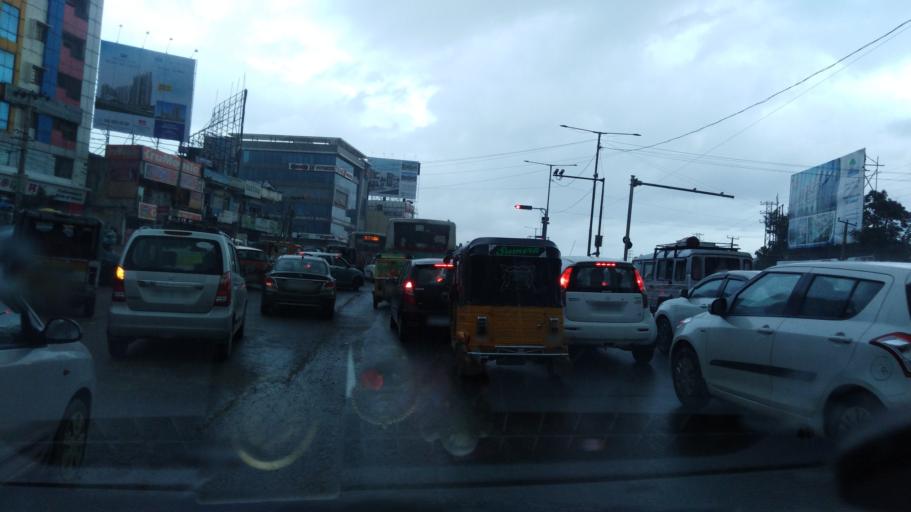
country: IN
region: Telangana
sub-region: Rangareddi
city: Kukatpalli
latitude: 17.4967
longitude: 78.3607
